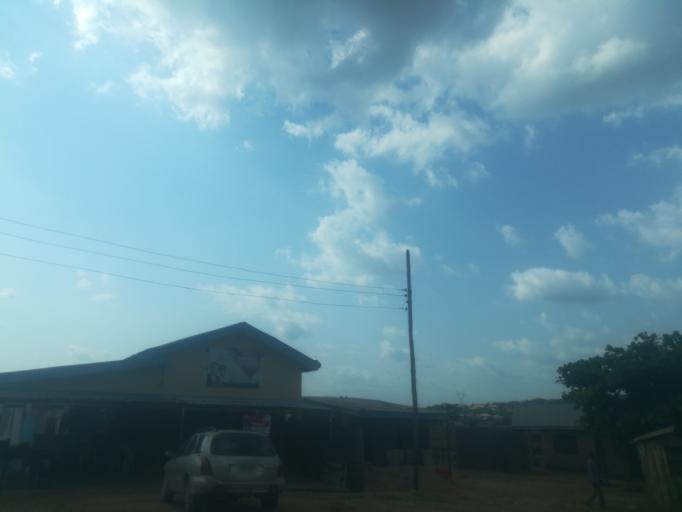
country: NG
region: Oyo
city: Moniya
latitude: 7.5143
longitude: 3.9130
